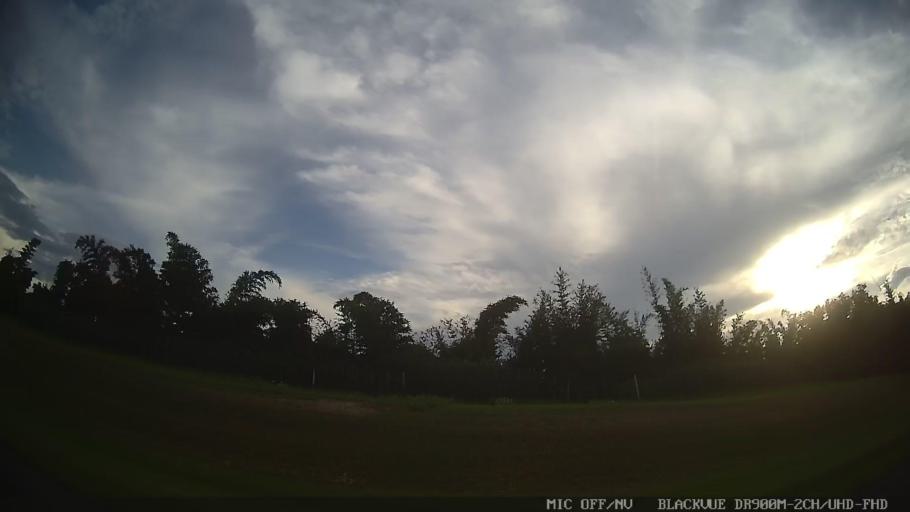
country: BR
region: Sao Paulo
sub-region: Porto Feliz
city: Porto Feliz
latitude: -23.1998
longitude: -47.6071
